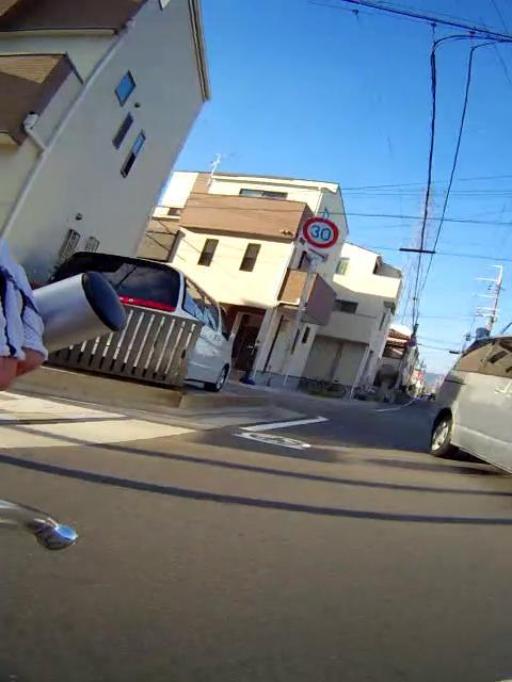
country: JP
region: Hyogo
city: Itami
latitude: 34.7733
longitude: 135.3833
